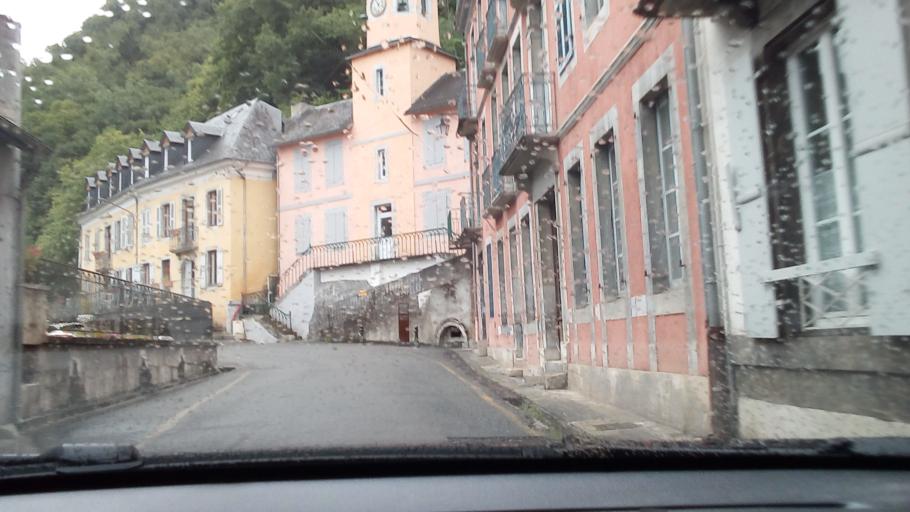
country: FR
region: Midi-Pyrenees
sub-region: Departement des Hautes-Pyrenees
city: Luz-Saint-Sauveur
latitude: 42.8641
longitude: -0.0117
